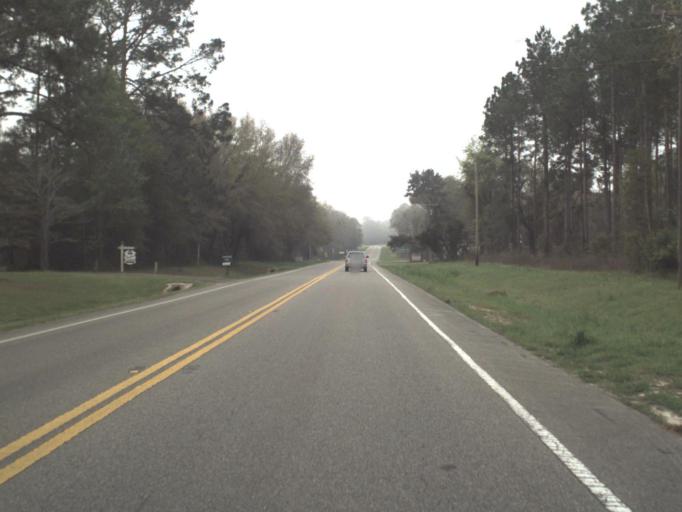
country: US
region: Florida
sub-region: Gadsden County
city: Gretna
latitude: 30.5505
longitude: -84.6769
